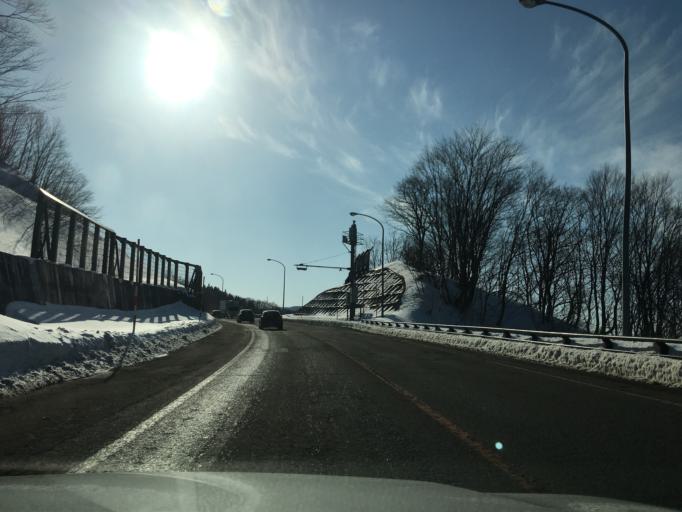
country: JP
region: Yamagata
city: Tsuruoka
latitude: 38.5621
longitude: 139.9349
